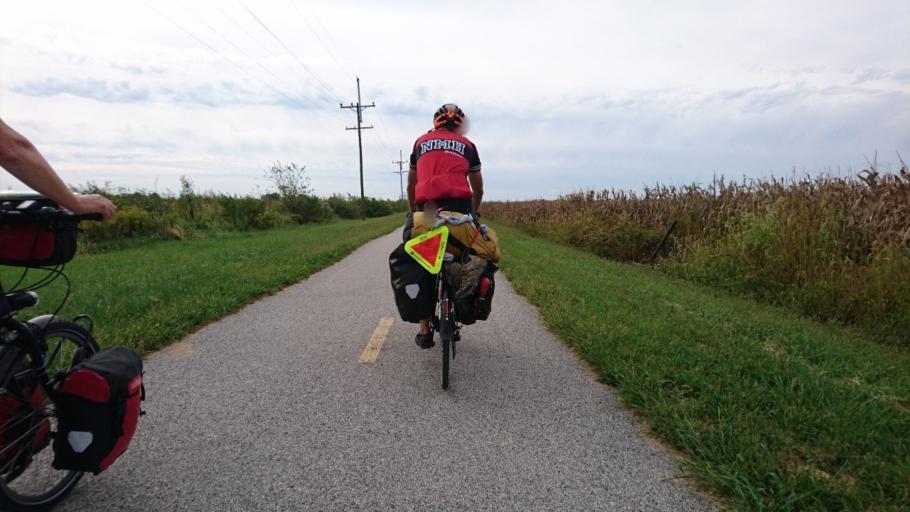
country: US
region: Illinois
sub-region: Madison County
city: Worden
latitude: 38.9074
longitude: -89.8379
